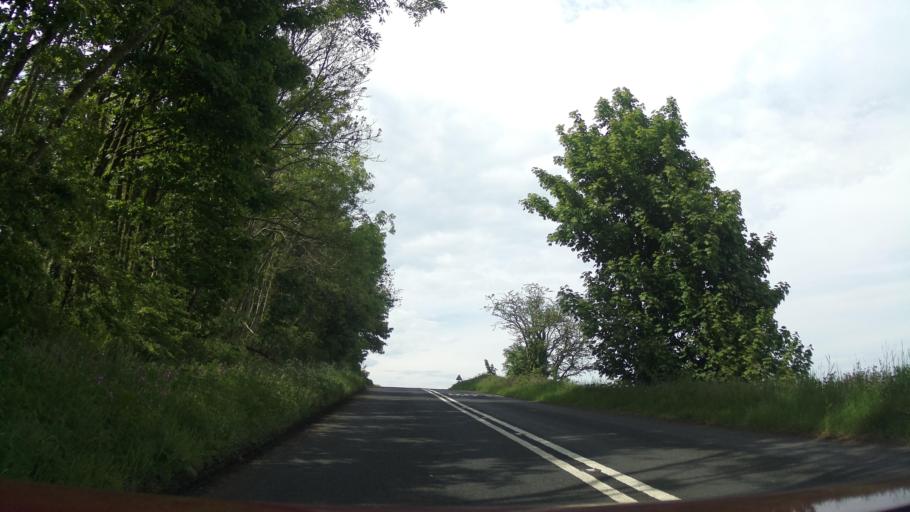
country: GB
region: England
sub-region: Northumberland
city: Alnwick
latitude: 55.4390
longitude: -1.7084
